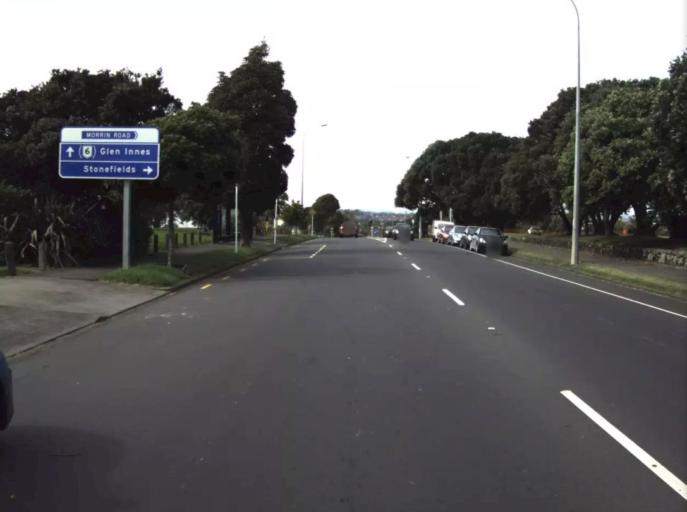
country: NZ
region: Auckland
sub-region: Auckland
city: Tamaki
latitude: -36.8800
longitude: 174.8494
